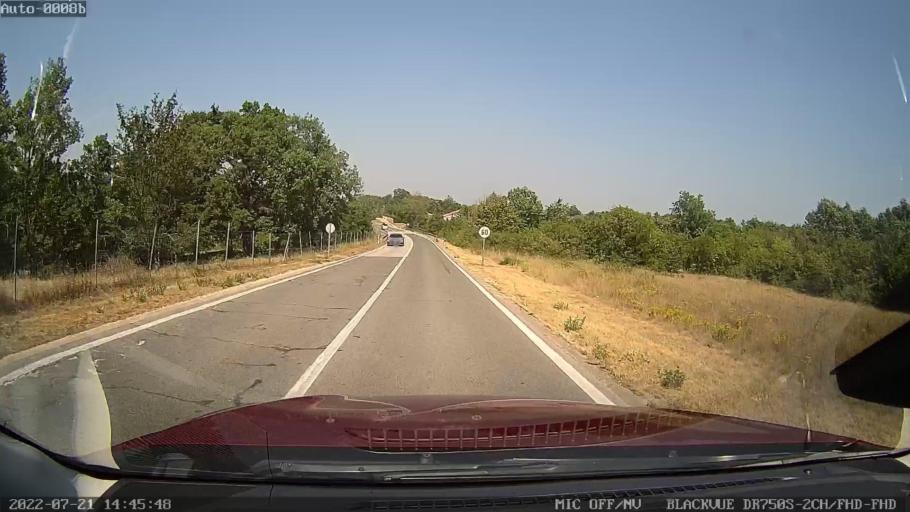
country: HR
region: Istarska
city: Pazin
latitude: 45.1316
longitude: 13.8950
